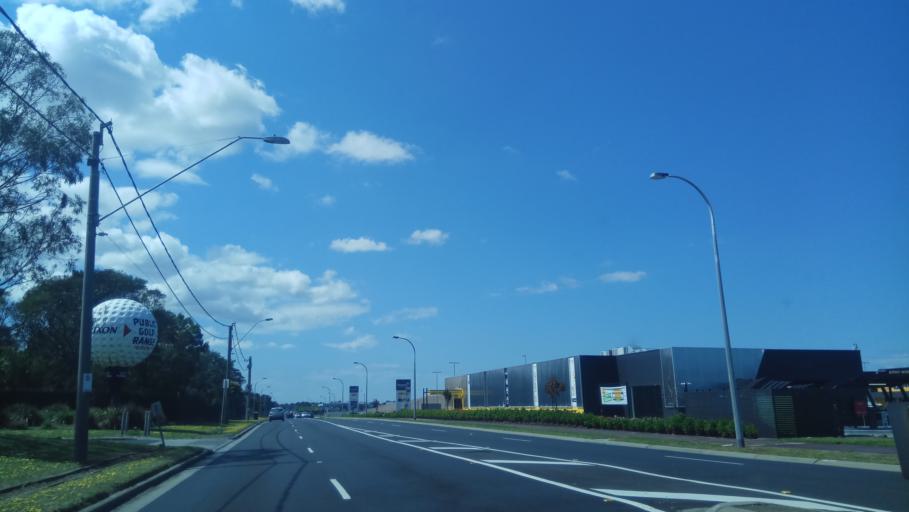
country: AU
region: Victoria
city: Heatherton
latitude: -37.9704
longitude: 145.0921
